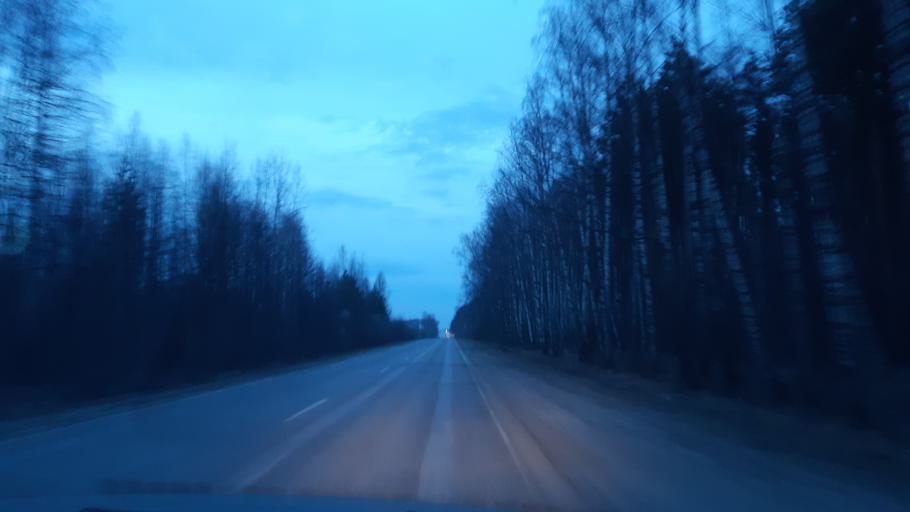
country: RU
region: Vladimir
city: Luknovo
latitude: 56.2274
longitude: 42.0348
